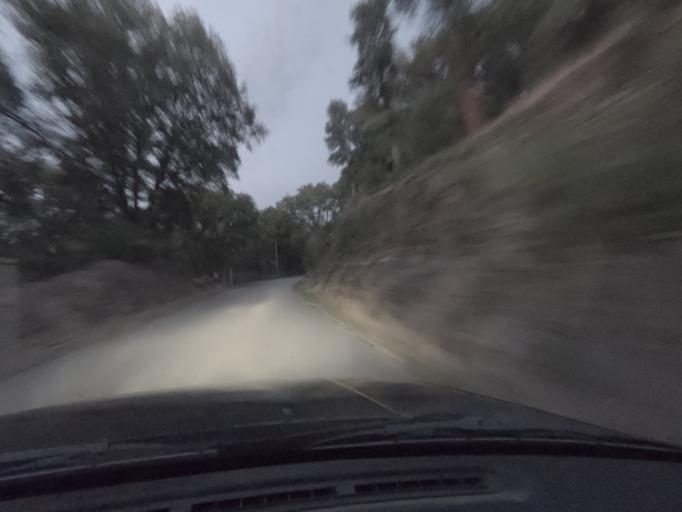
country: PT
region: Vila Real
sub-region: Peso da Regua
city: Godim
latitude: 41.1631
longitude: -7.8377
